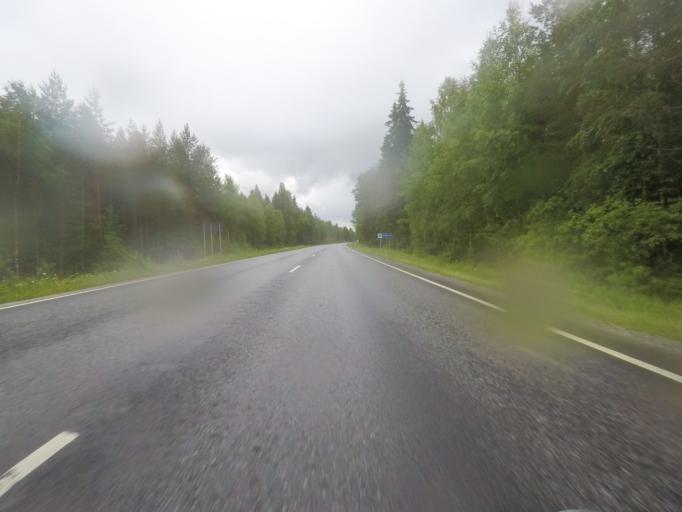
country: FI
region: Central Finland
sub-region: Jyvaeskylae
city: Toivakka
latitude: 62.2268
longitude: 26.1986
